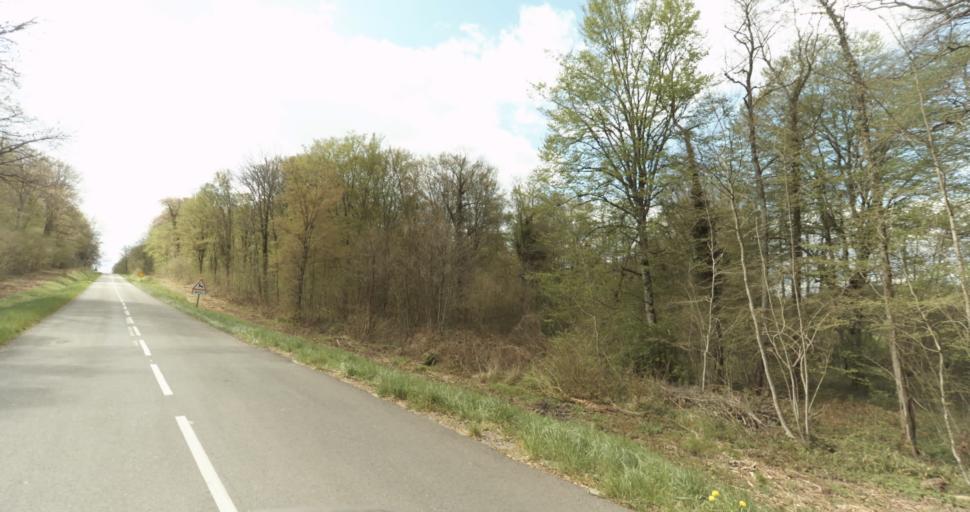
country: FR
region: Bourgogne
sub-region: Departement de la Cote-d'Or
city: Auxonne
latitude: 47.1938
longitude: 5.4521
